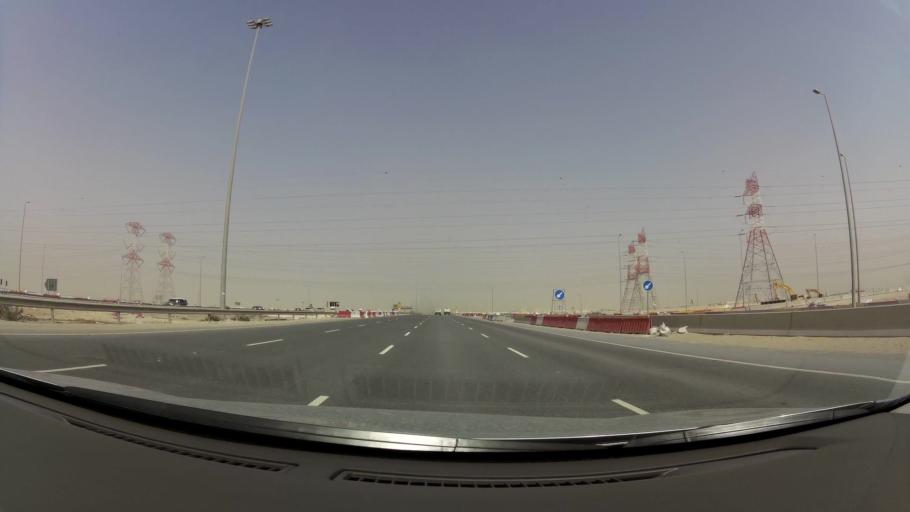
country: QA
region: Baladiyat ar Rayyan
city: Ar Rayyan
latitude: 25.1739
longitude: 51.3312
